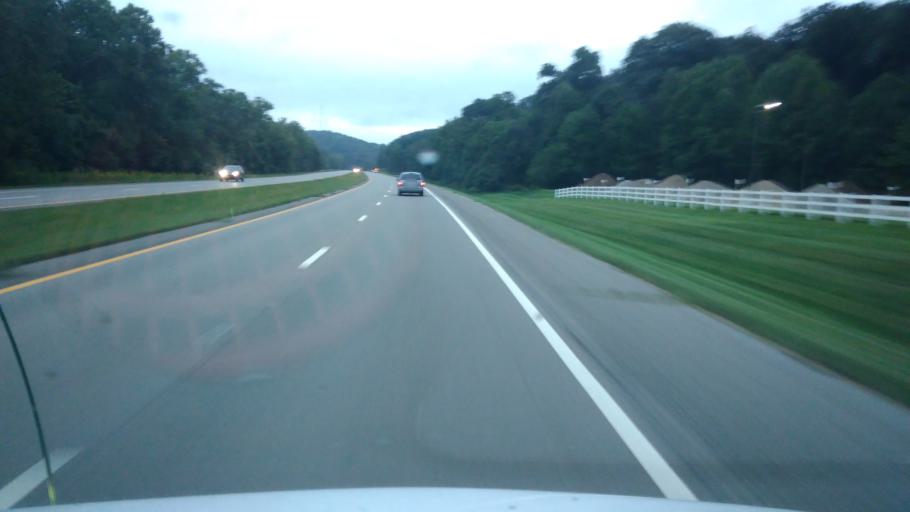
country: US
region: Ohio
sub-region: Ross County
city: Chillicothe
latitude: 39.2553
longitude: -82.9773
